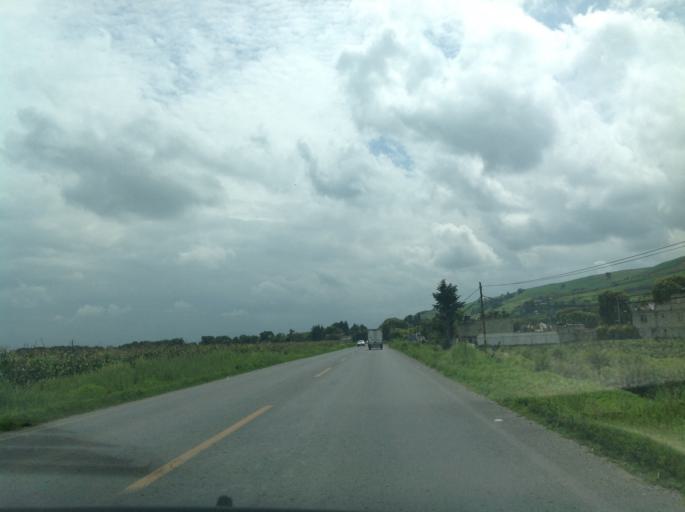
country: MX
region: Morelos
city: Tenango de Arista
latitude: 19.1085
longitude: -99.5739
